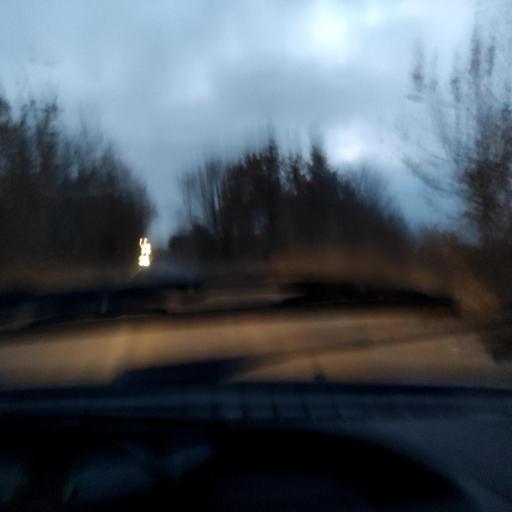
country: RU
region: Samara
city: Tol'yatti
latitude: 53.5688
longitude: 49.4795
